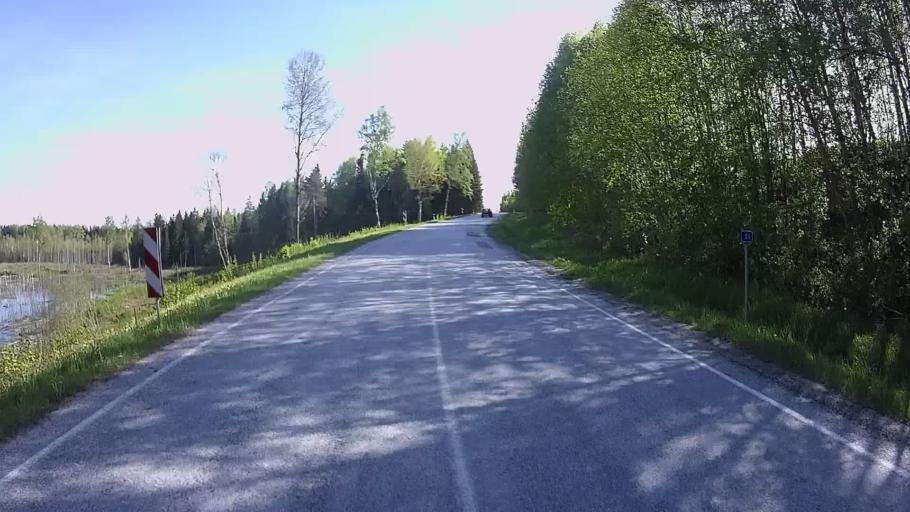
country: EE
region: Vorumaa
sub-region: Antsla vald
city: Vana-Antsla
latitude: 58.0172
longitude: 26.4999
